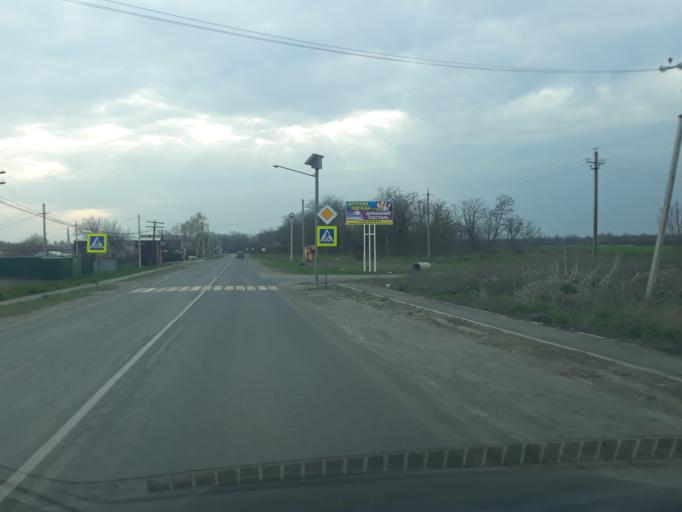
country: RU
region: Rostov
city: Novobessergenovka
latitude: 47.1797
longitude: 38.8001
